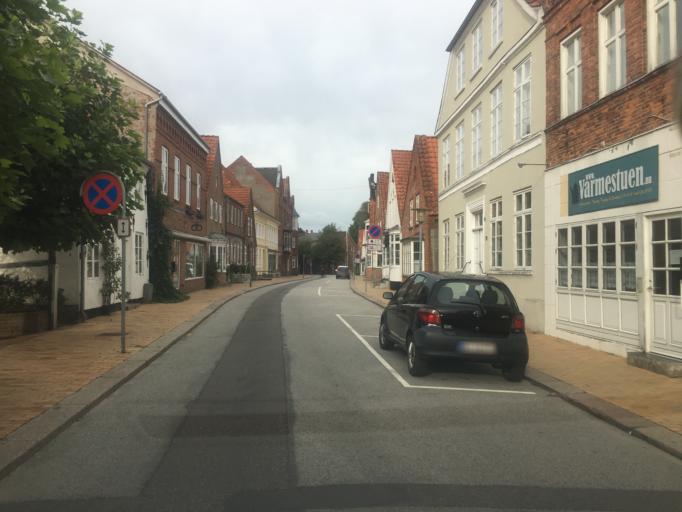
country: DK
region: South Denmark
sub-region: Tonder Kommune
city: Tonder
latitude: 54.9370
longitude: 8.8726
